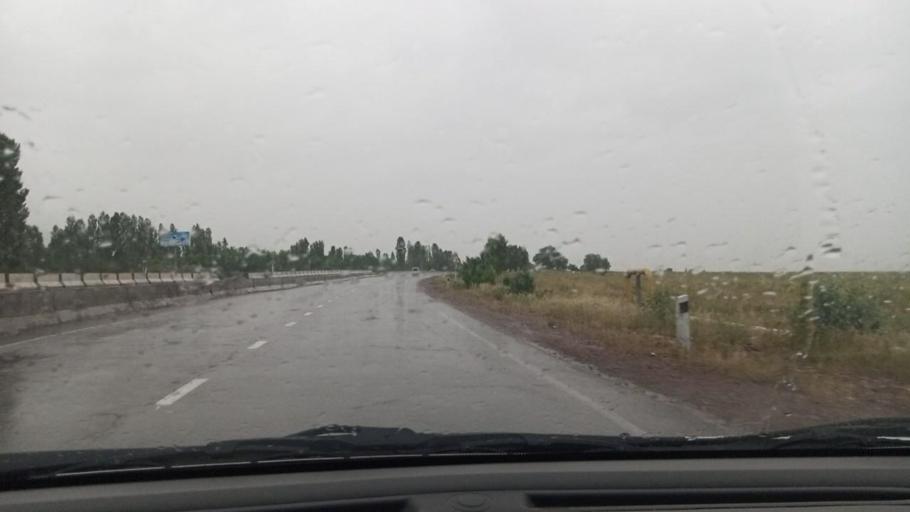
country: UZ
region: Toshkent
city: Angren
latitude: 40.9474
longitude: 69.9088
